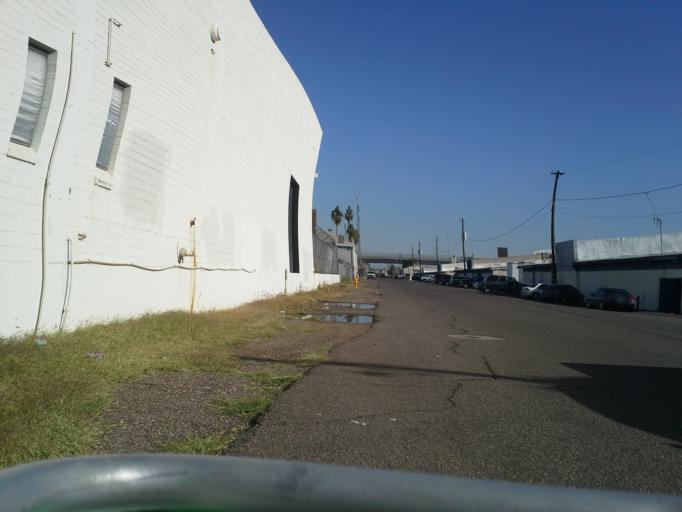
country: US
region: Arizona
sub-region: Maricopa County
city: Phoenix
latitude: 33.4452
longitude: -112.0519
